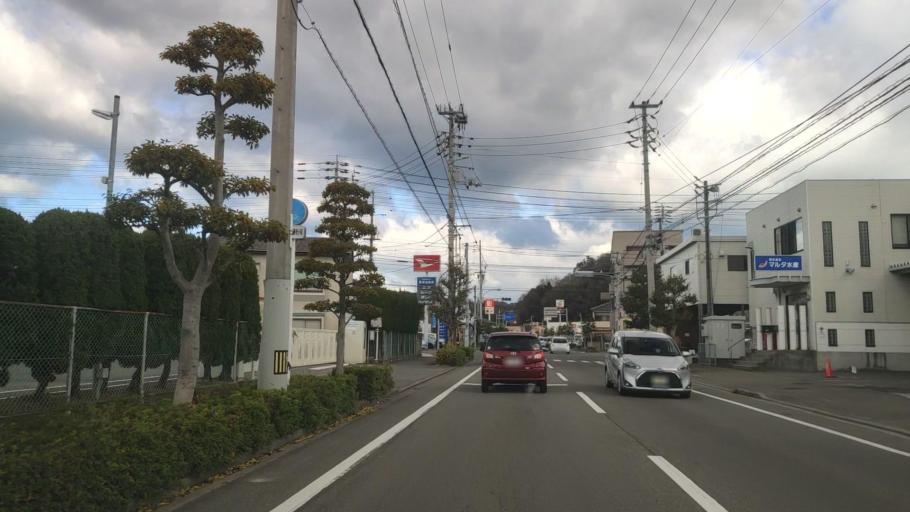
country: JP
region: Ehime
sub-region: Shikoku-chuo Shi
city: Matsuyama
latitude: 33.8660
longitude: 132.7252
